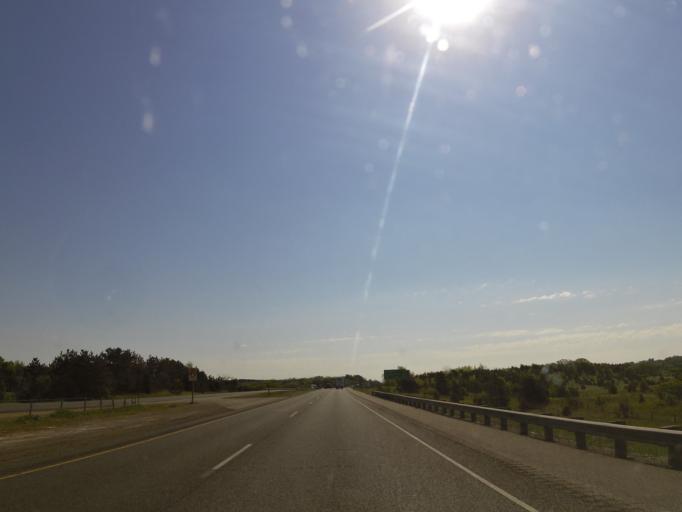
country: US
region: Wisconsin
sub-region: Saint Croix County
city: Hudson
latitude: 44.9650
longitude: -92.6634
